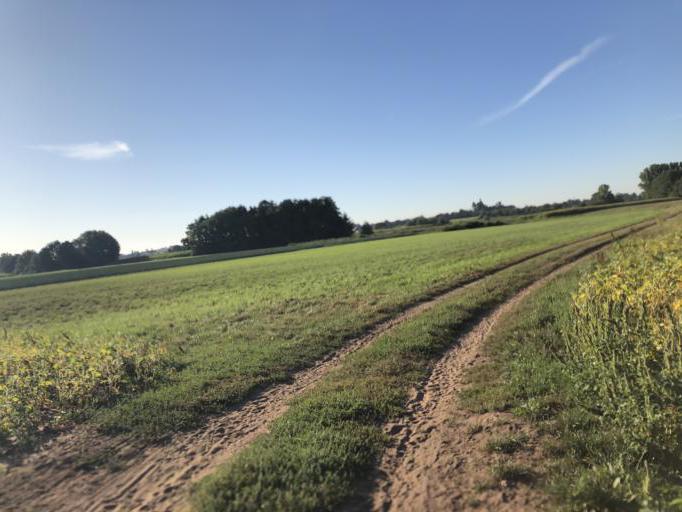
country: DE
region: Bavaria
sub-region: Regierungsbezirk Mittelfranken
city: Erlangen
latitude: 49.5395
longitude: 11.0061
